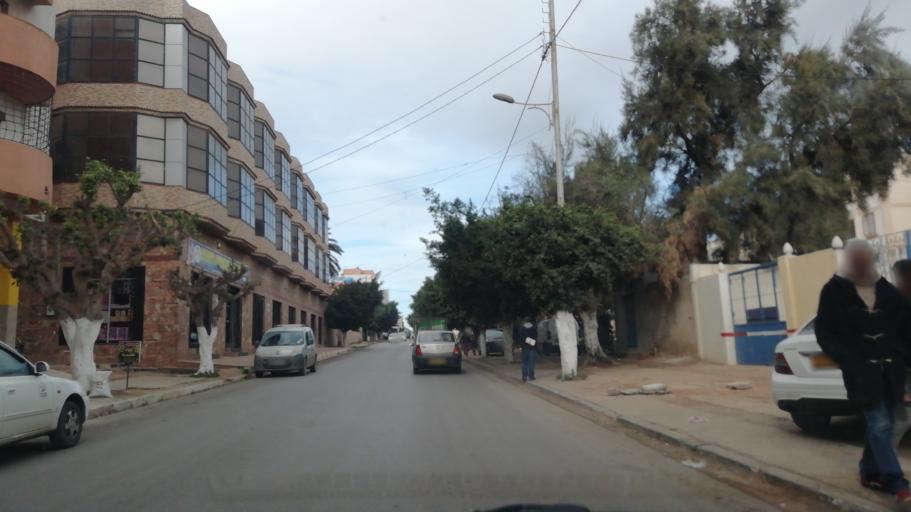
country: DZ
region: Oran
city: Oran
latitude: 35.6854
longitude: -0.6168
